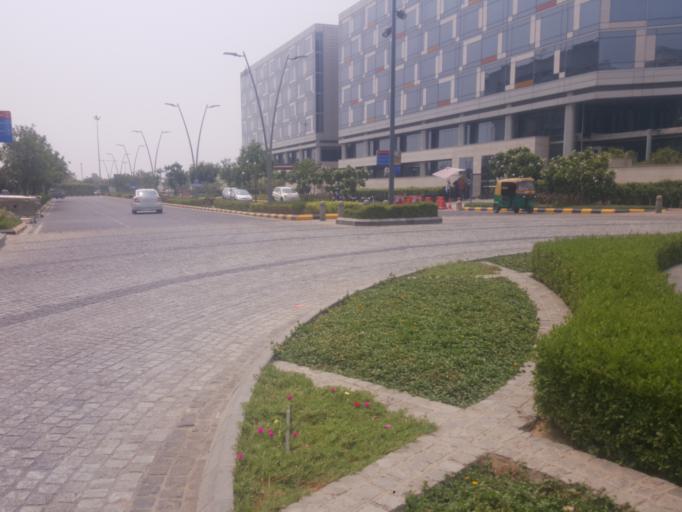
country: IN
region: NCT
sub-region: Central Delhi
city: Karol Bagh
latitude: 28.5531
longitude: 77.1228
